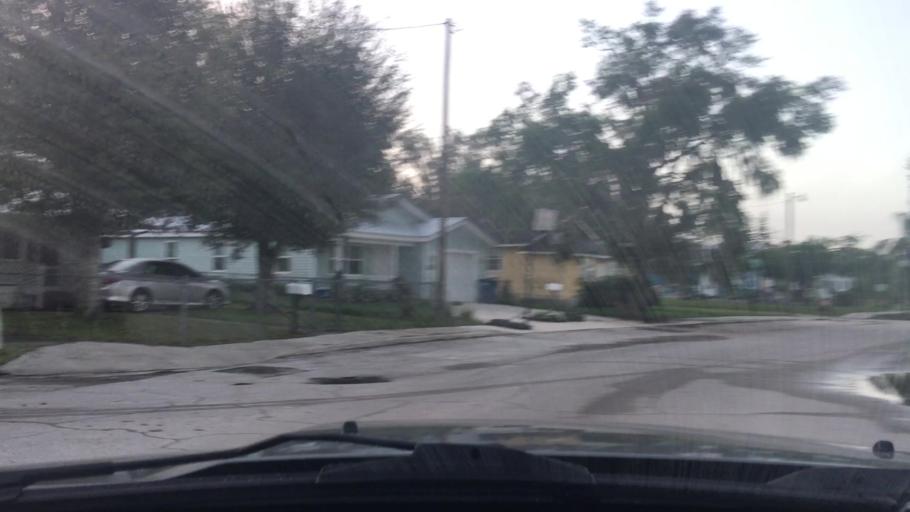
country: US
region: Florida
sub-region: Highlands County
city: Sebring
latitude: 27.4957
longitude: -81.4380
